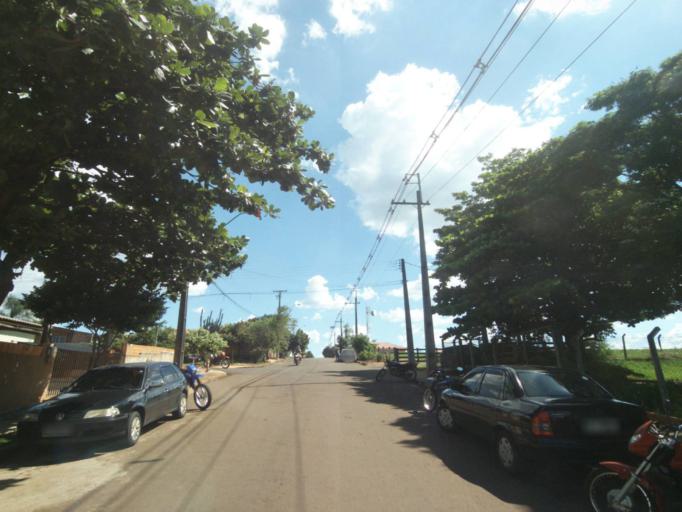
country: BR
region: Parana
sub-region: Sertanopolis
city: Sertanopolis
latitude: -23.0403
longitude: -50.8217
